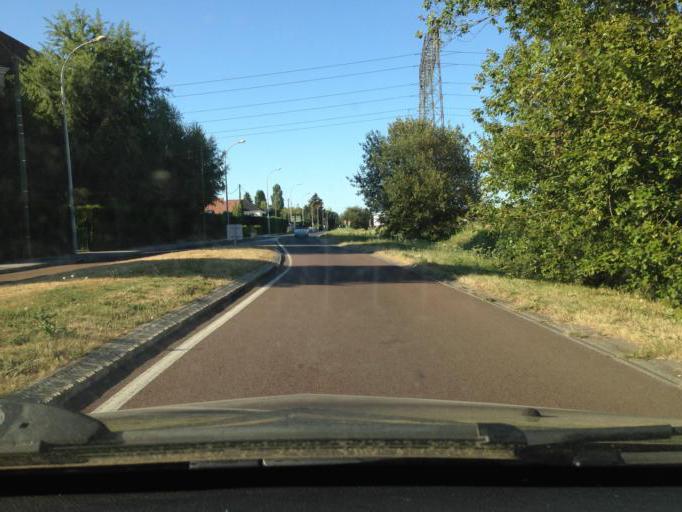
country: FR
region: Ile-de-France
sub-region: Departement des Yvelines
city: Saint-Remy-les-Chevreuse
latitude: 48.7160
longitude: 2.0860
